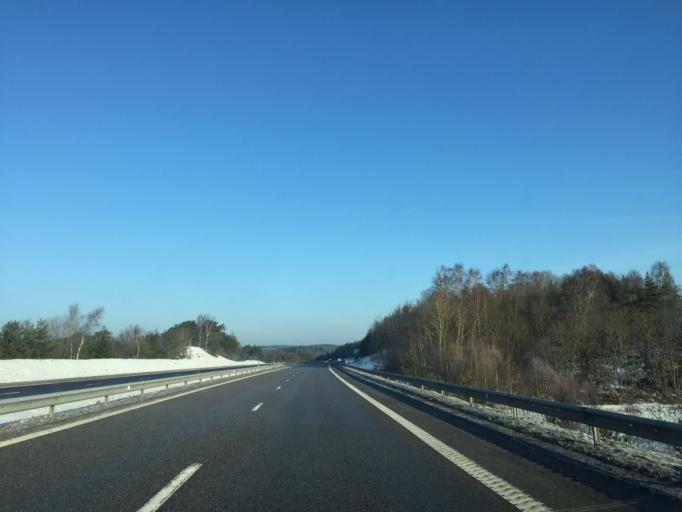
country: SE
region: Vaestra Goetaland
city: Svanesund
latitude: 58.0922
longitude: 11.8823
